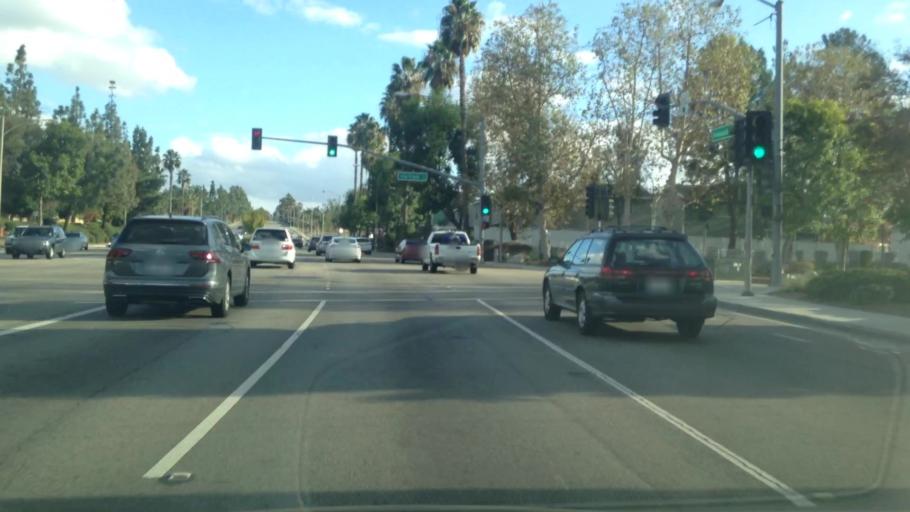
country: US
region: California
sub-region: Riverside County
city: Woodcrest
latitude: 33.9318
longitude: -117.3487
